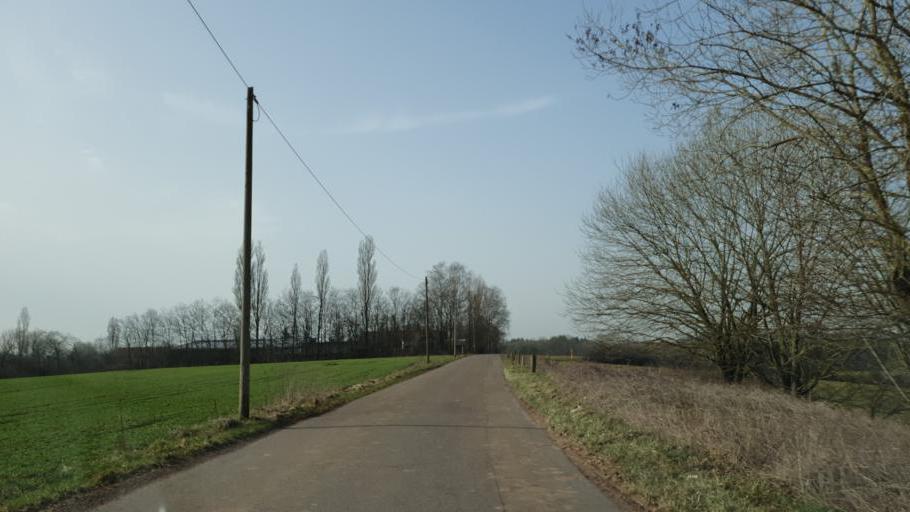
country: DE
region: Saarland
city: Schmelz
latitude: 49.4409
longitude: 6.8030
